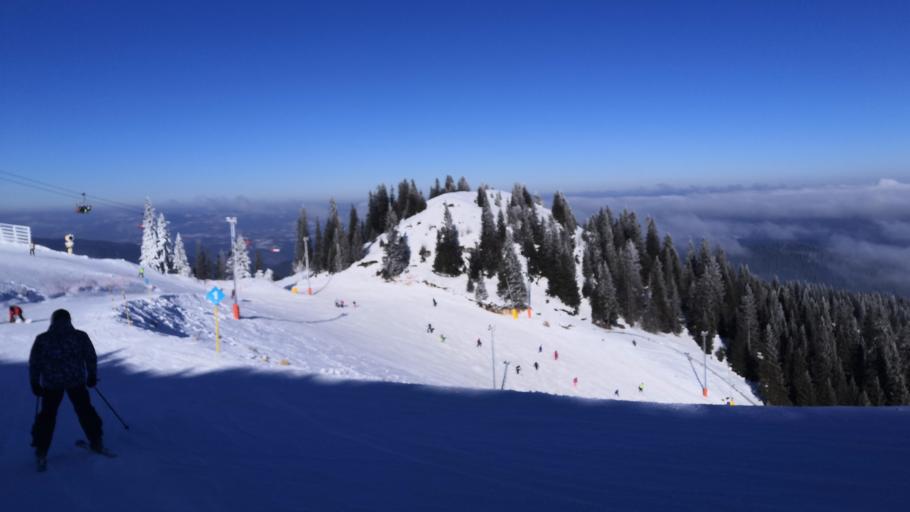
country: BA
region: Republika Srpska
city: Koran
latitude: 43.7236
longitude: 18.5619
